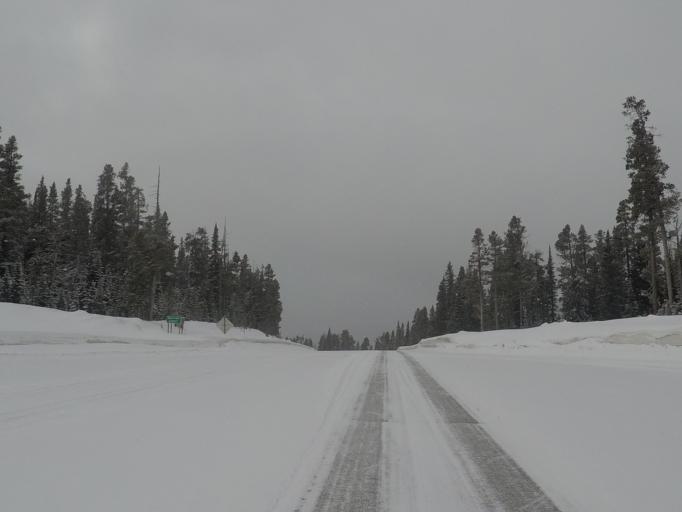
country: US
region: Montana
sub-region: Meagher County
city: White Sulphur Springs
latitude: 46.8412
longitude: -110.6951
